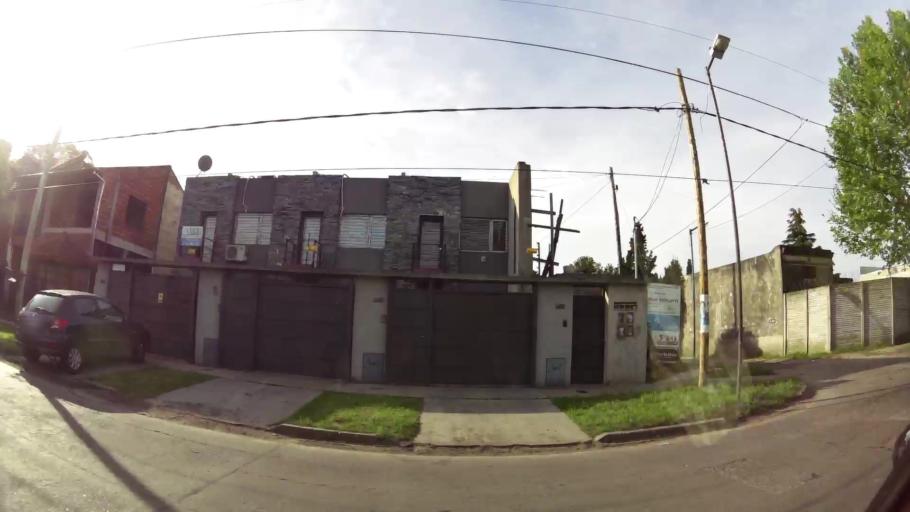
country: AR
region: Buenos Aires
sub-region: Partido de Quilmes
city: Quilmes
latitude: -34.7396
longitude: -58.2552
